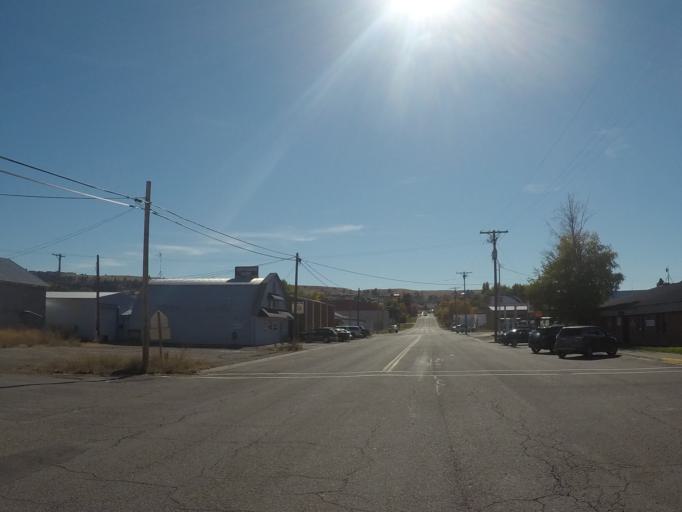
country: US
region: Montana
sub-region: Lake County
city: Polson
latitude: 47.6884
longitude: -114.1634
